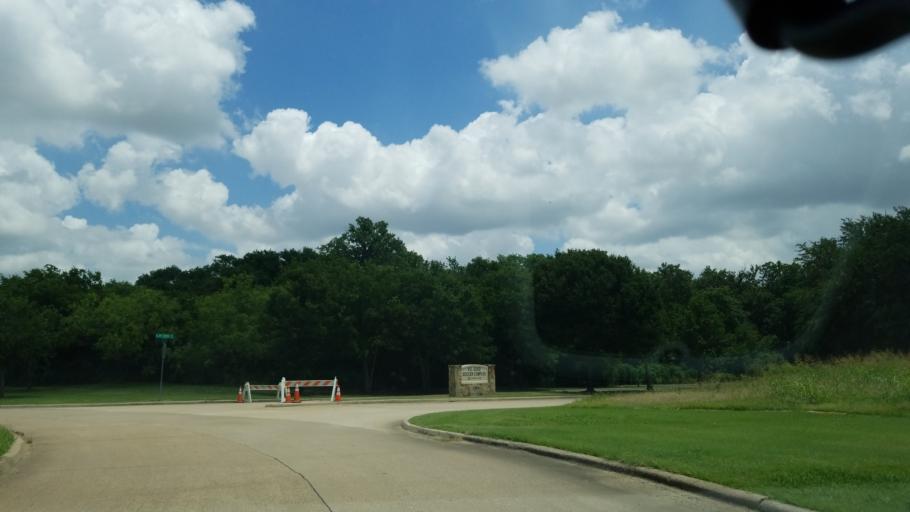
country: US
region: Texas
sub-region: Dallas County
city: Carrollton
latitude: 32.9562
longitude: -96.9375
